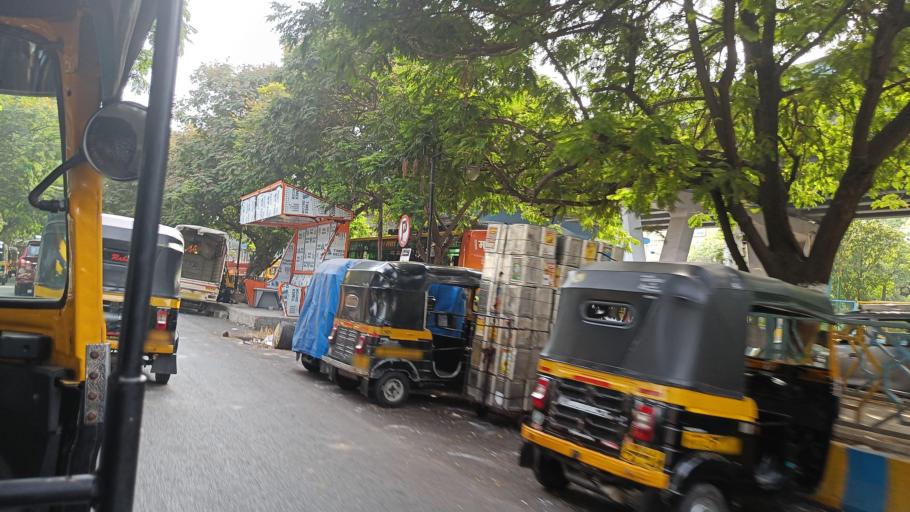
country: IN
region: Maharashtra
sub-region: Thane
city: Thane
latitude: 19.2025
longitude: 72.9673
